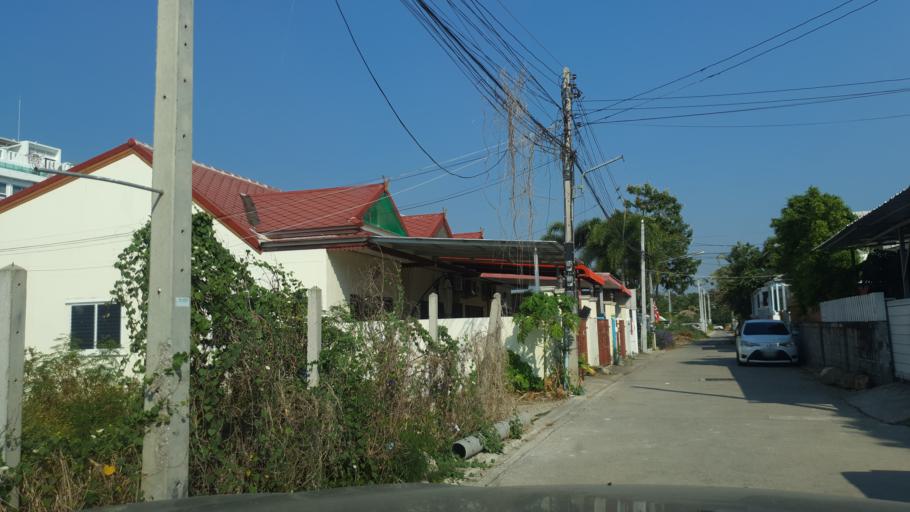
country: TH
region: Prachuap Khiri Khan
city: Hua Hin
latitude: 12.5524
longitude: 99.9552
